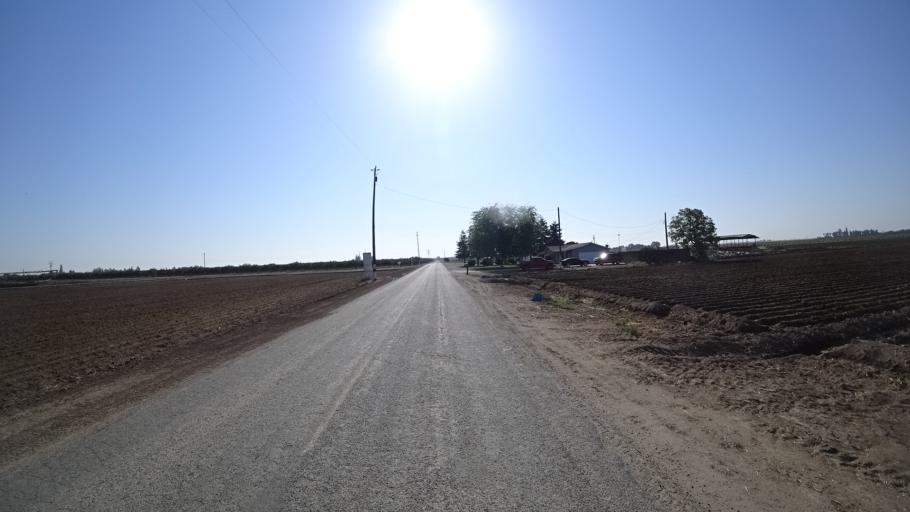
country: US
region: California
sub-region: Kings County
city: Lucerne
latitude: 36.3935
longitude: -119.6839
